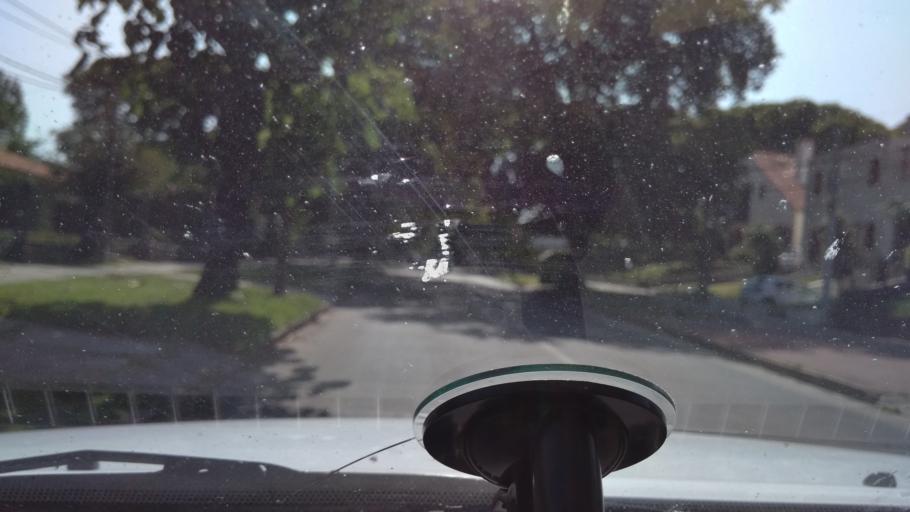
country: UY
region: Canelones
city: Paso de Carrasco
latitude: -34.8908
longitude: -56.0752
